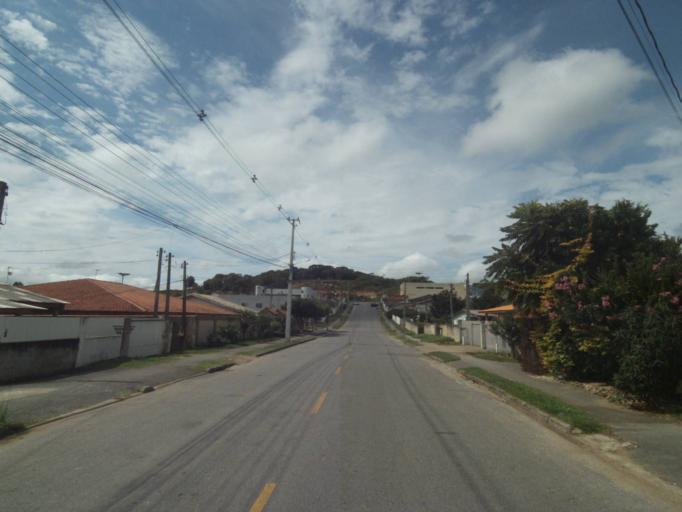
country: BR
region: Parana
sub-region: Quatro Barras
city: Quatro Barras
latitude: -25.3451
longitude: -49.0759
